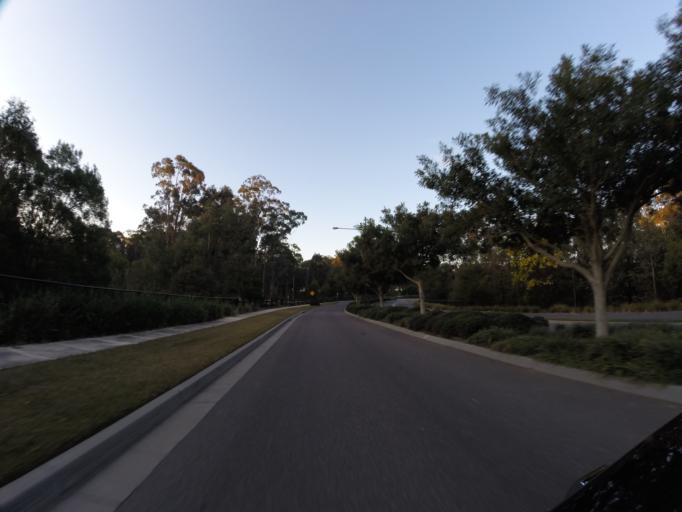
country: AU
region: New South Wales
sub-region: Camden
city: Narellan
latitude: -34.0194
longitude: 150.7413
